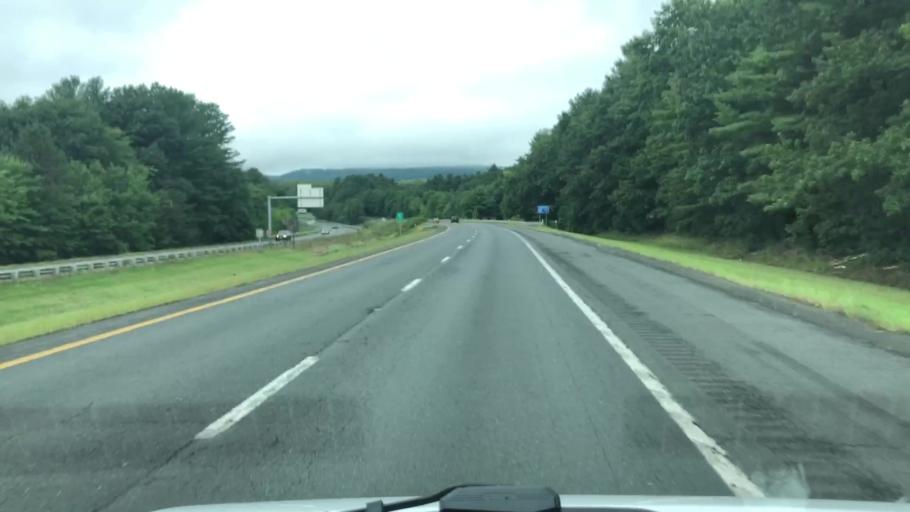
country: US
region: Massachusetts
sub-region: Hampden County
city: Westfield
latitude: 42.1525
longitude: -72.7519
